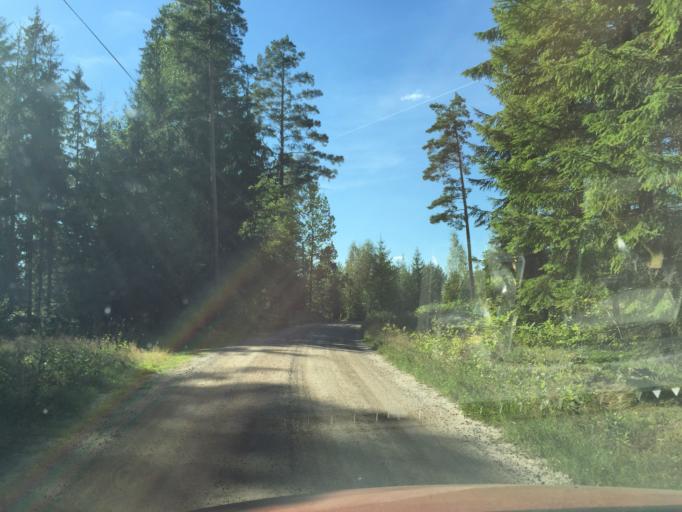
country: SE
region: OEstergoetland
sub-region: Finspangs Kommun
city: Finspang
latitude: 58.8869
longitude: 15.7435
